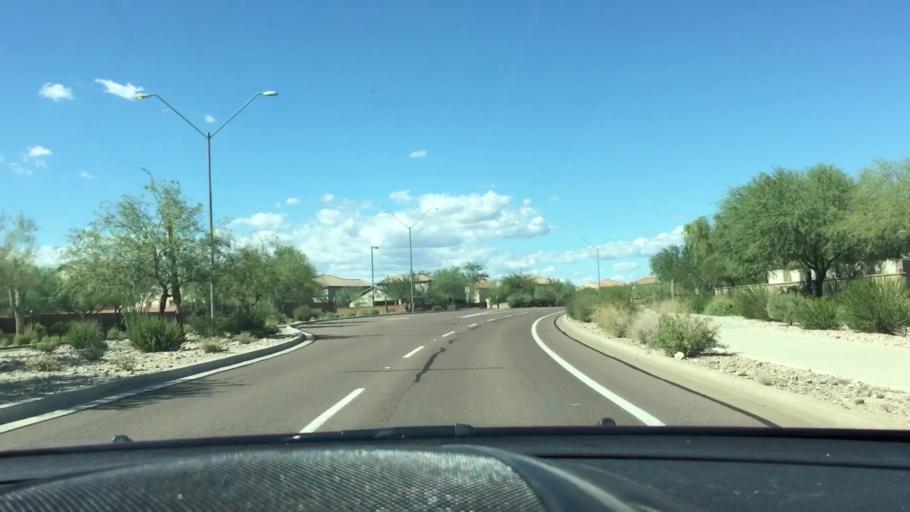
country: US
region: Arizona
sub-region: Maricopa County
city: Sun City West
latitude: 33.7314
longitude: -112.2529
